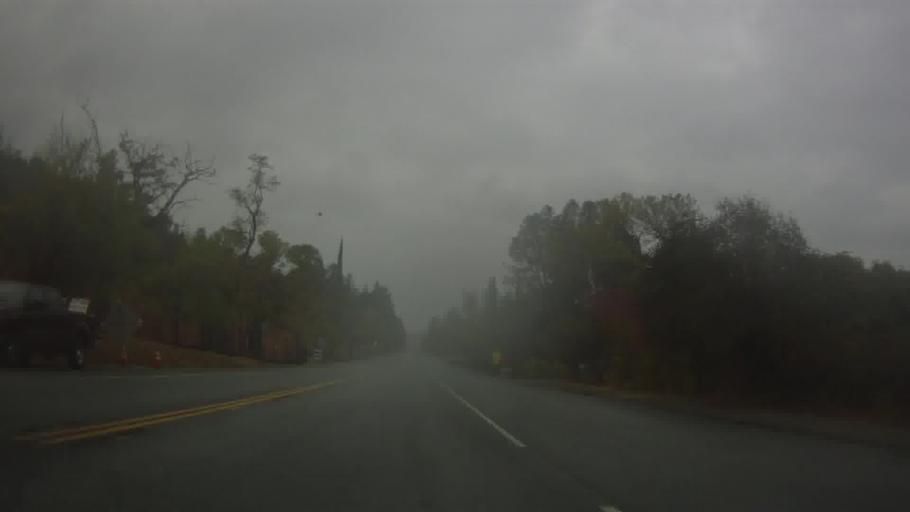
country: US
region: California
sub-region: Shasta County
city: Shasta
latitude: 40.5982
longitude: -122.4908
